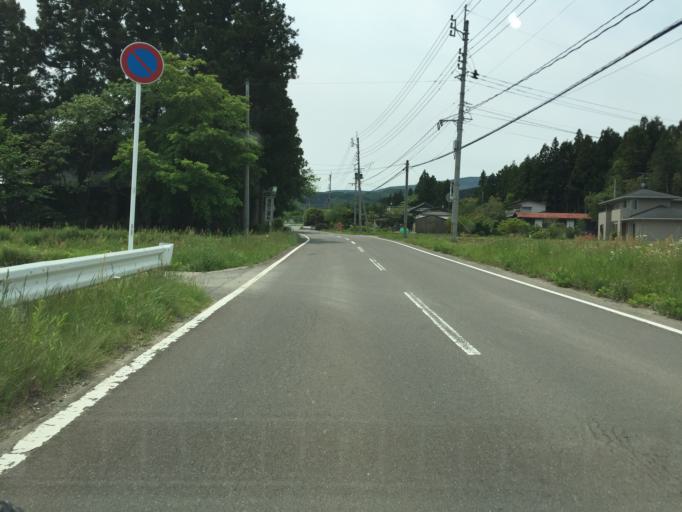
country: JP
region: Fukushima
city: Fukushima-shi
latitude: 37.7137
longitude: 140.3519
